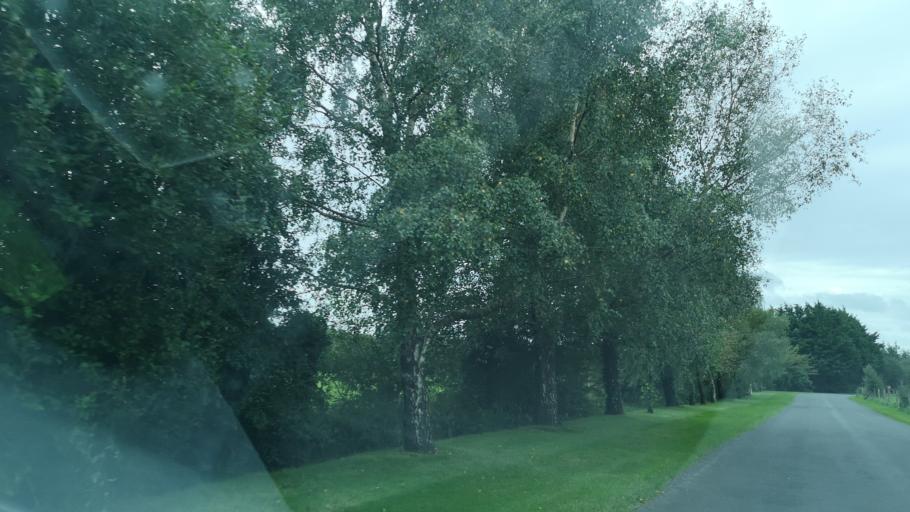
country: IE
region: Leinster
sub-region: Uibh Fhaili
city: Ferbane
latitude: 53.2270
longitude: -7.7292
